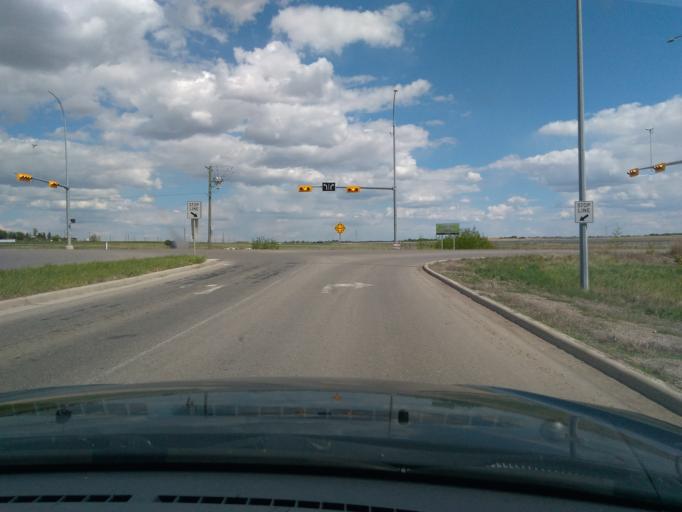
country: CA
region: Alberta
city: Chestermere
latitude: 50.9474
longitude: -113.9124
